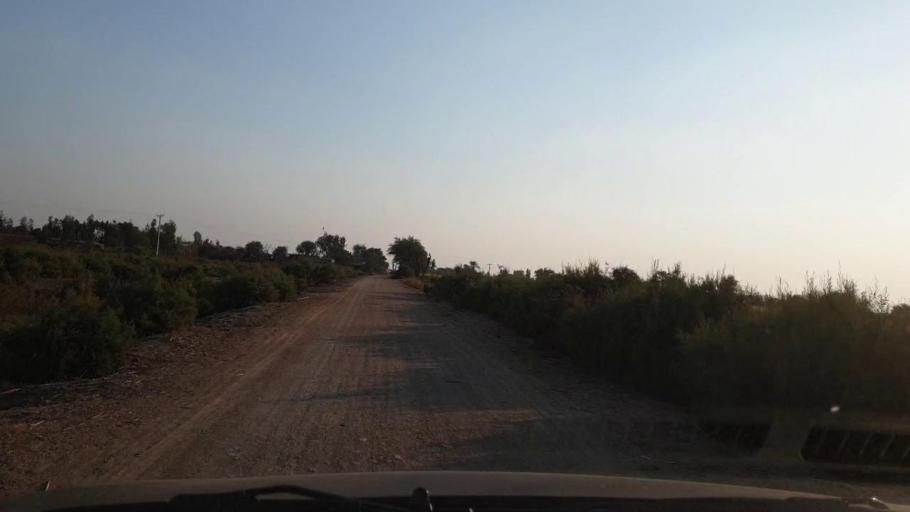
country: PK
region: Sindh
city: Jhol
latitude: 25.9297
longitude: 68.9176
